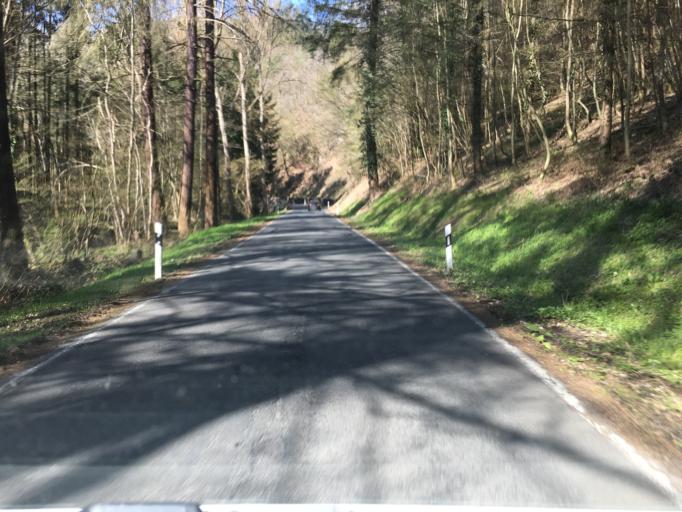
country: DE
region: Rheinland-Pfalz
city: Lind
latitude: 50.5160
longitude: 6.9562
